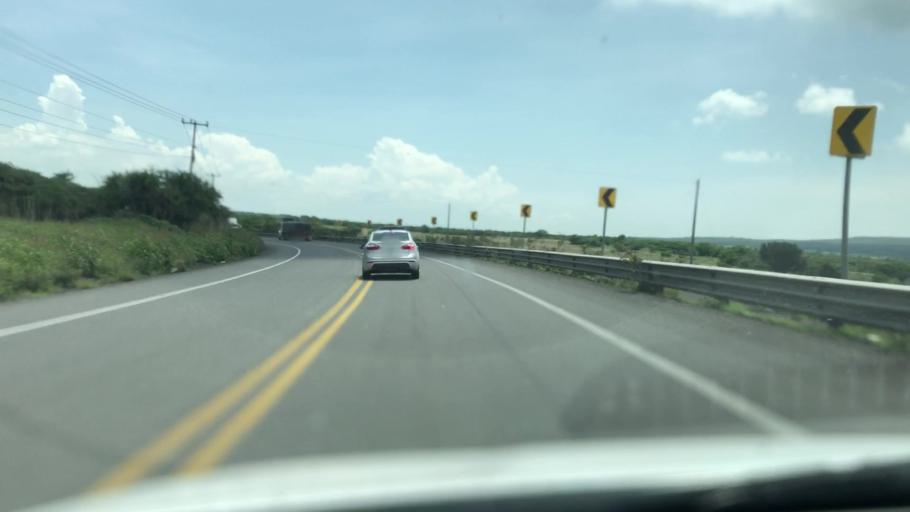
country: MX
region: Michoacan
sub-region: Yurecuaro
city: Yurecuaro
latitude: 20.3425
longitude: -102.1625
